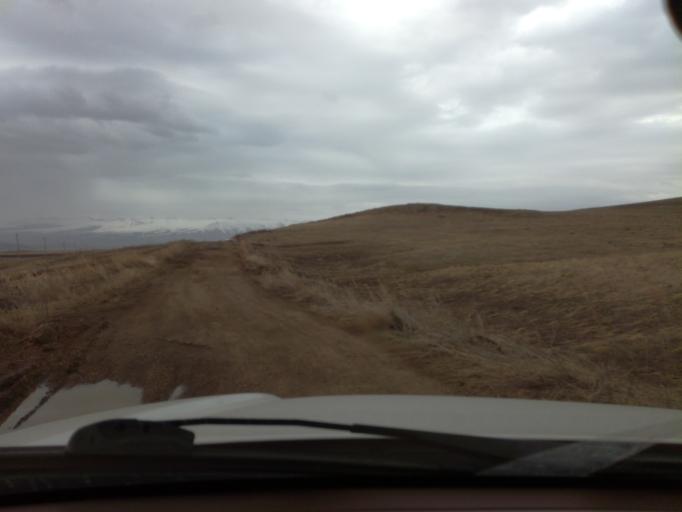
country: AM
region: Shirak
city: Amasia
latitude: 41.0199
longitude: 43.7044
